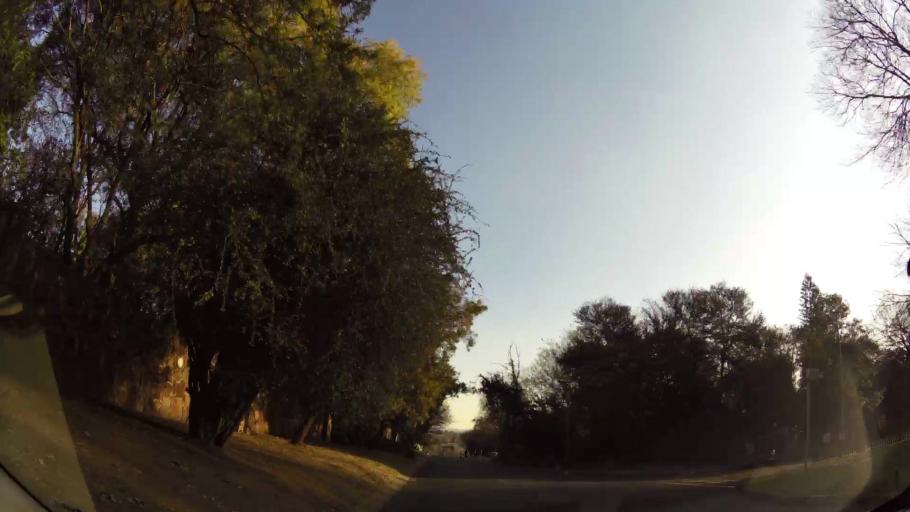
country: ZA
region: Gauteng
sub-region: City of Johannesburg Metropolitan Municipality
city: Diepsloot
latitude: -26.0643
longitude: 27.9909
